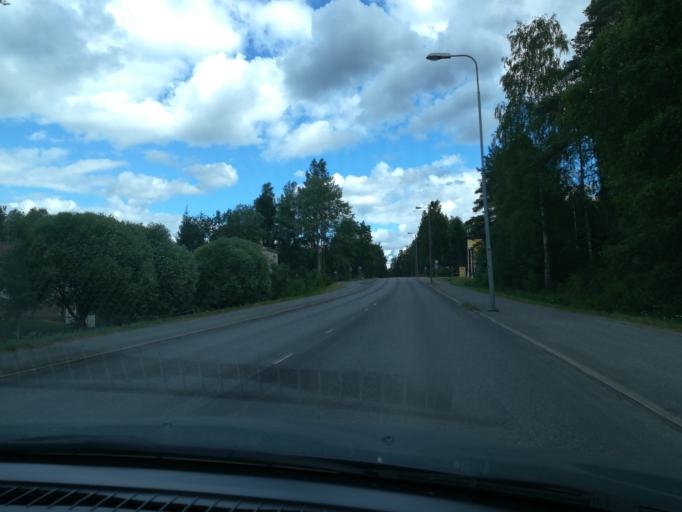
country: FI
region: Southern Savonia
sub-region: Mikkeli
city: Maentyharju
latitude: 61.4200
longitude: 26.8903
